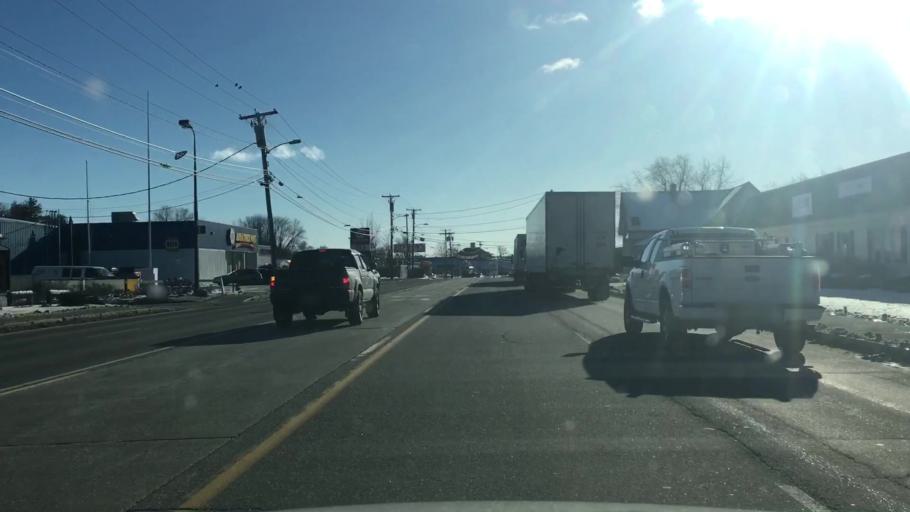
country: US
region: Maine
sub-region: Androscoggin County
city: Lewiston
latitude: 44.1146
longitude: -70.2245
